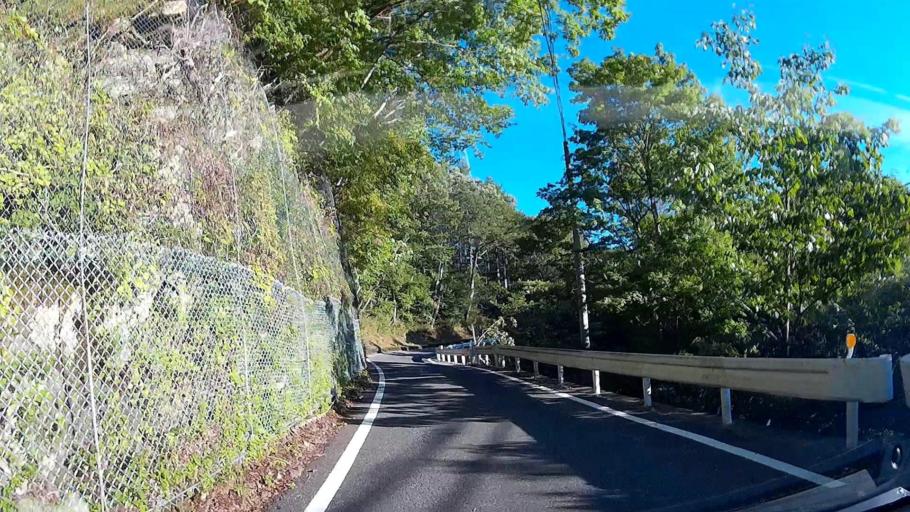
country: JP
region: Shizuoka
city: Shizuoka-shi
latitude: 35.1999
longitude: 138.2525
